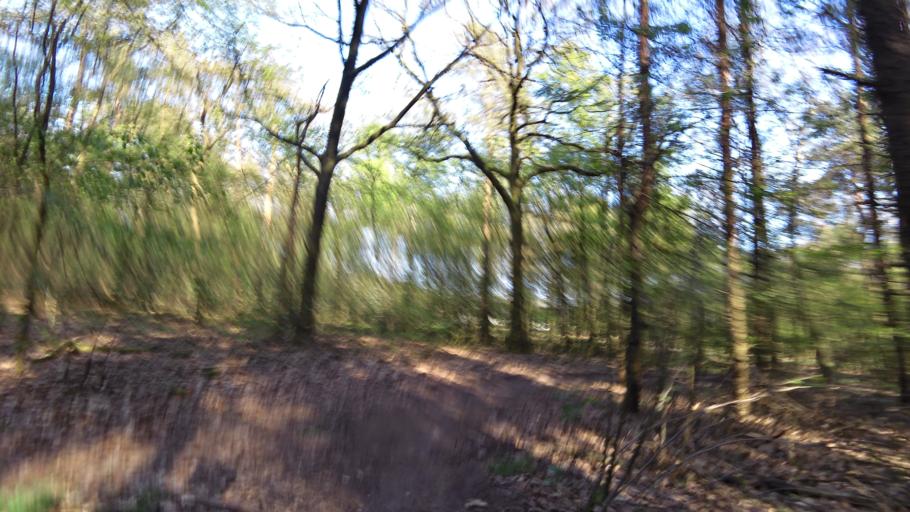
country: NL
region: Gelderland
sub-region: Gemeente Renkum
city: Wolfheze
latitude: 52.0103
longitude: 5.8147
